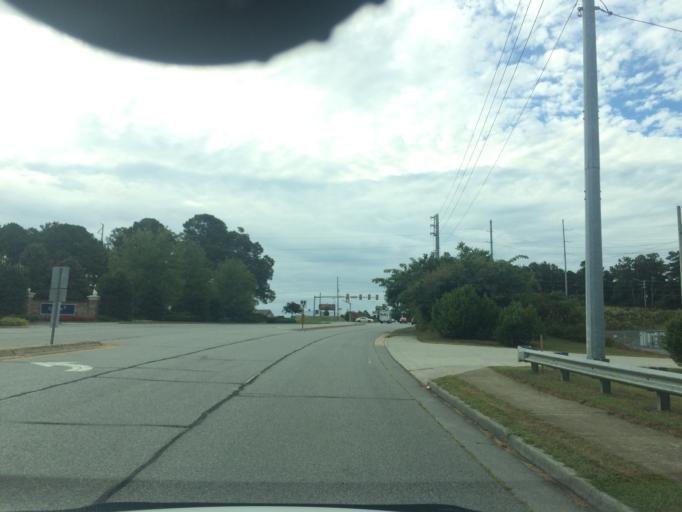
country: US
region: Georgia
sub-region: Cobb County
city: Kennesaw
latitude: 34.0509
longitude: -84.5850
